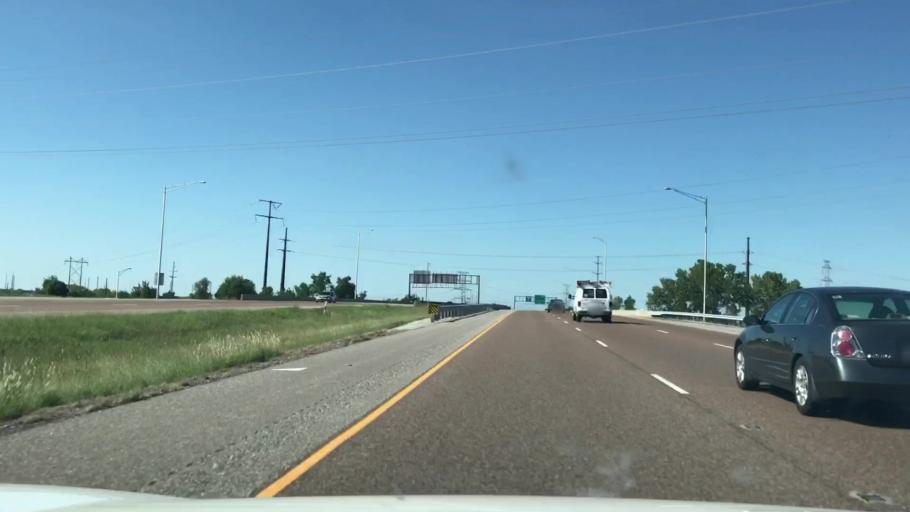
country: US
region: Illinois
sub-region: Madison County
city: Pontoon Beach
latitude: 38.7315
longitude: -90.0379
